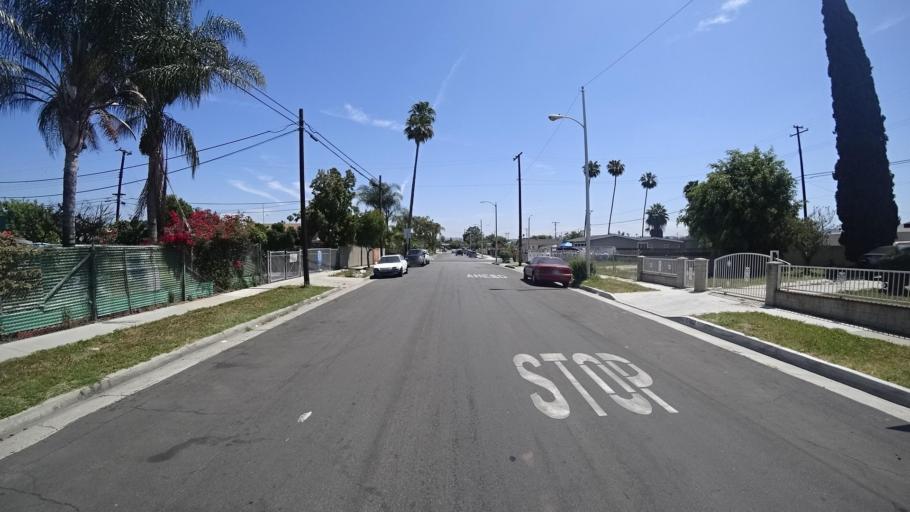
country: US
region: California
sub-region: Los Angeles County
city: South San Jose Hills
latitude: 34.0094
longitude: -117.9131
